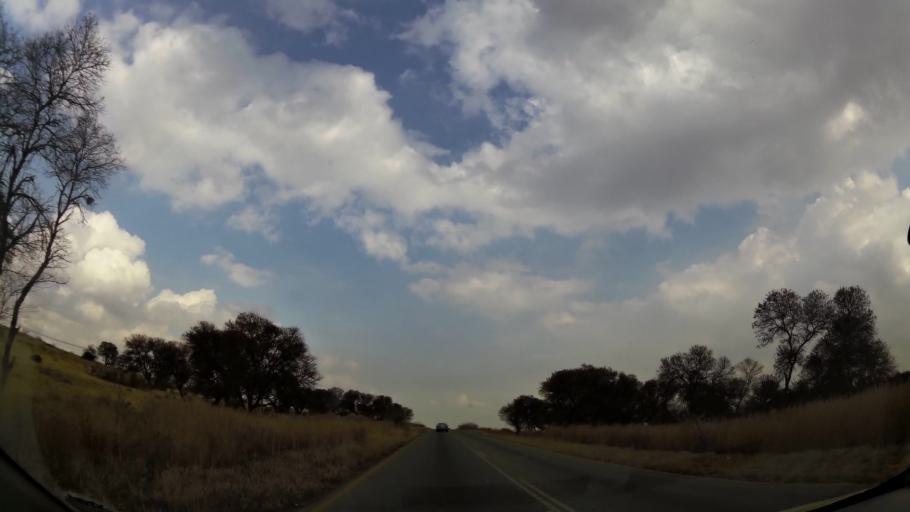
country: ZA
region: Orange Free State
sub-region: Fezile Dabi District Municipality
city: Sasolburg
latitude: -26.7863
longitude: 27.9176
